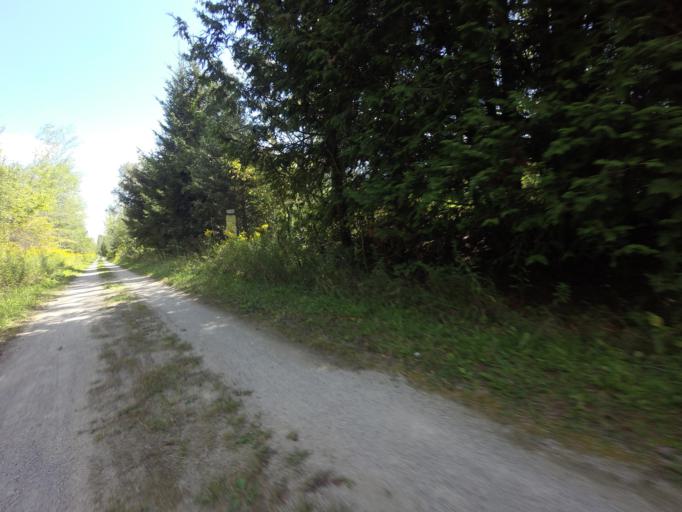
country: CA
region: Ontario
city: Orangeville
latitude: 43.7785
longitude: -80.1219
